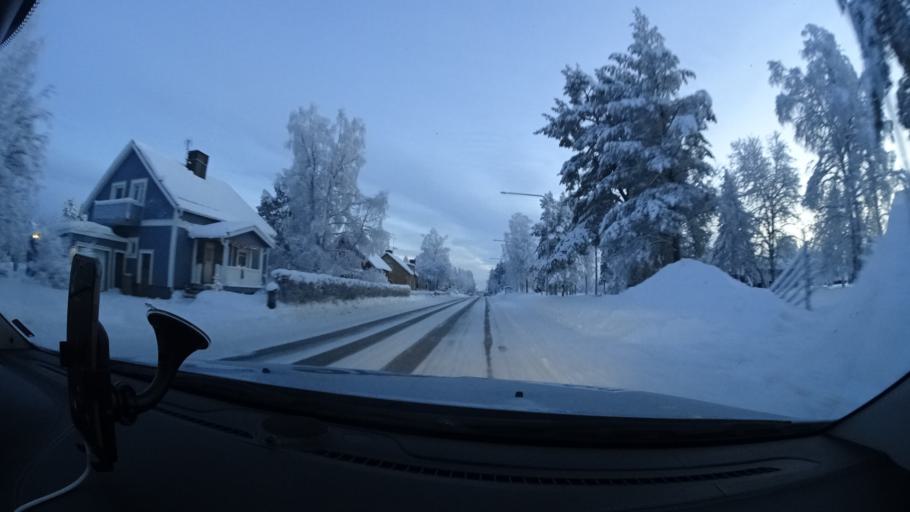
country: SE
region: Vaesterbotten
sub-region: Norsjo Kommun
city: Norsjoe
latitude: 64.9171
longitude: 19.4733
